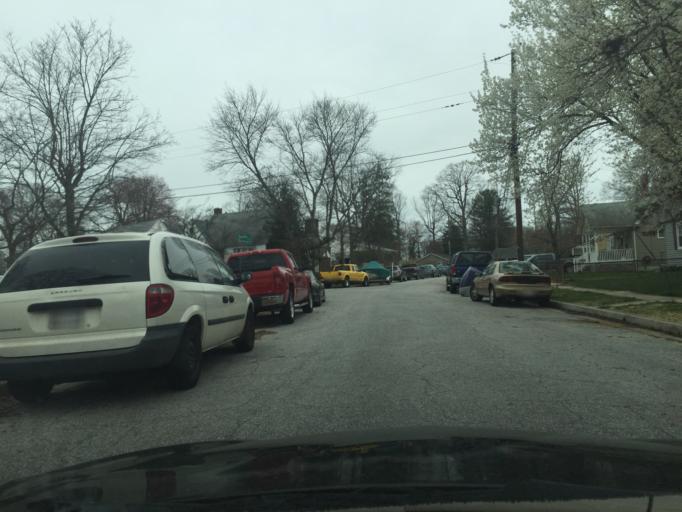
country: US
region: Maryland
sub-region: Baltimore County
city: Middle River
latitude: 39.3209
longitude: -76.4207
